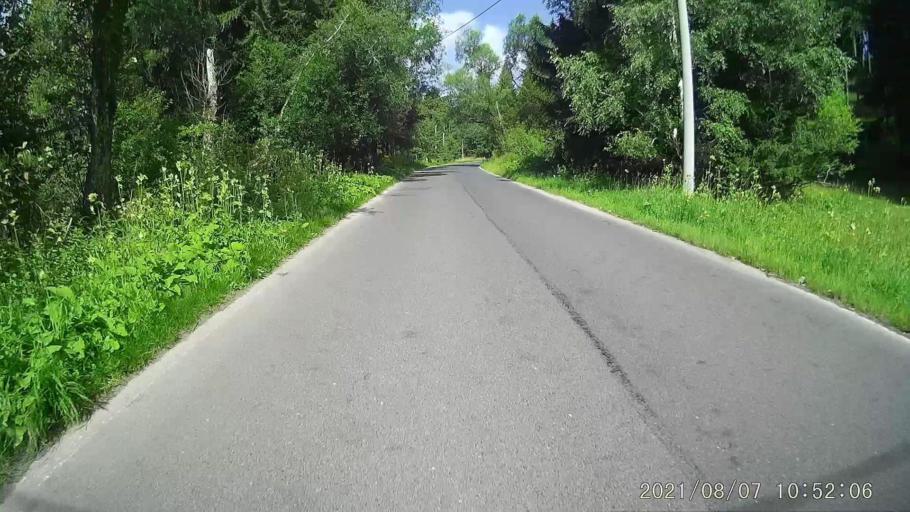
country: CZ
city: Rokytnice v Orlickych Horach
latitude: 50.2840
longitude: 16.4715
